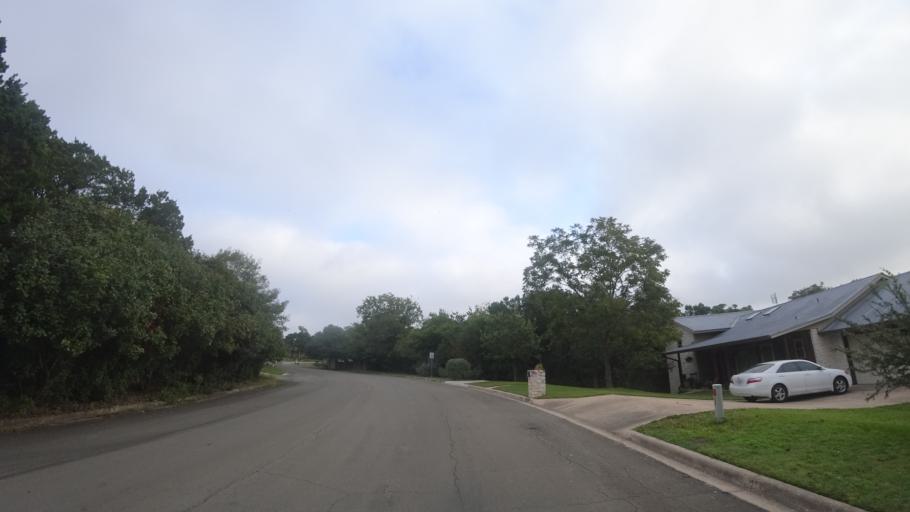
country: US
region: Texas
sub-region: Travis County
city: Wells Branch
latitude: 30.3670
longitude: -97.6650
